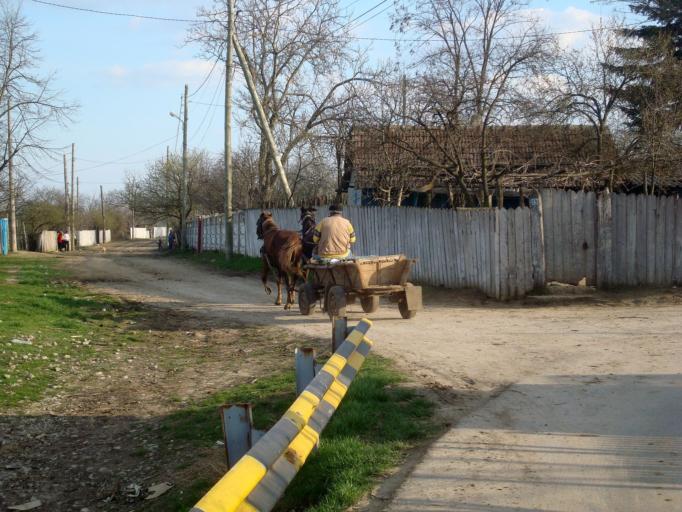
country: RO
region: Galati
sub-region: Comuna Radesti
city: Radesti
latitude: 46.0671
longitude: 27.7877
